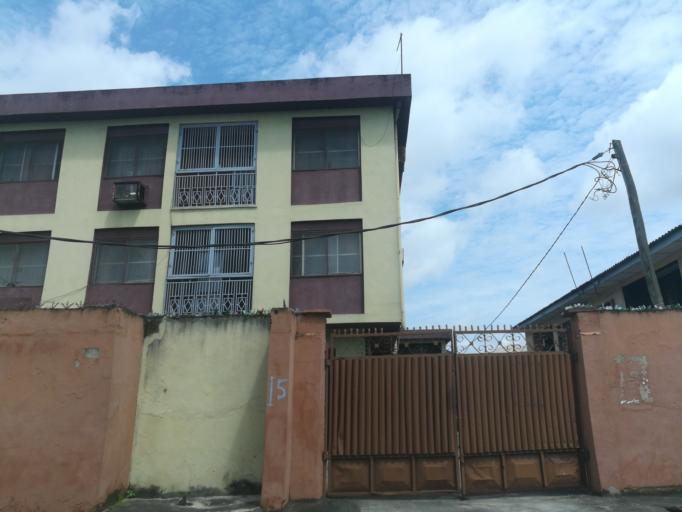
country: NG
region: Lagos
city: Somolu
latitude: 6.5283
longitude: 3.3830
